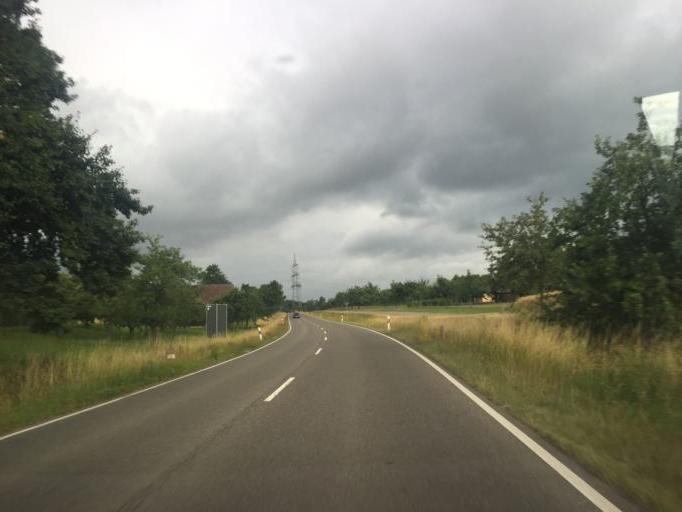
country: DE
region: Baden-Wuerttemberg
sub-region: Regierungsbezirk Stuttgart
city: Gartringen
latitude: 48.6430
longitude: 8.8793
